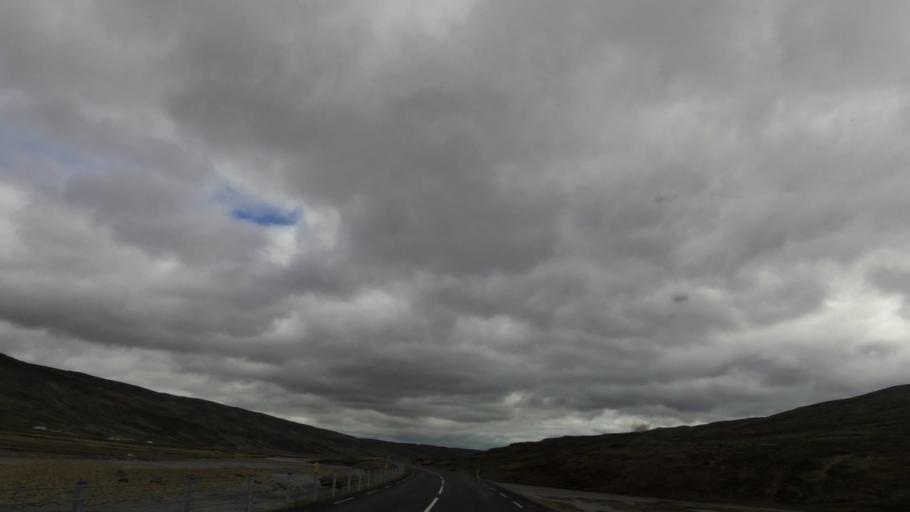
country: IS
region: West
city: Stykkisholmur
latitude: 65.7583
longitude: -21.8613
